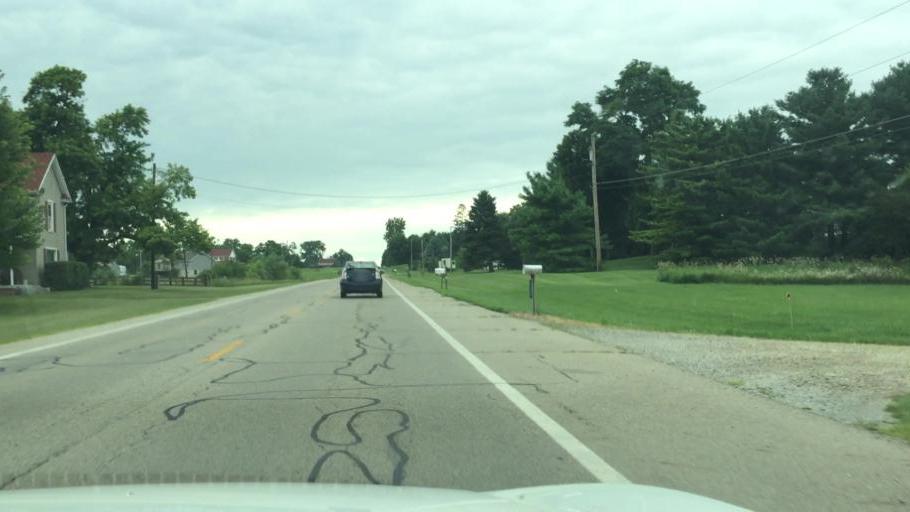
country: US
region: Ohio
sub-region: Champaign County
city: Mechanicsburg
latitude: 40.0784
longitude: -83.5991
